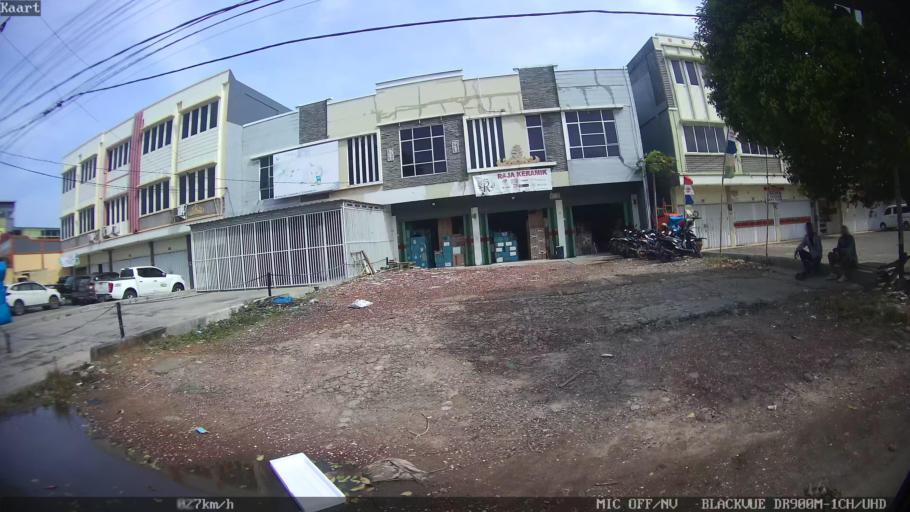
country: ID
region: Lampung
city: Kedaton
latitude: -5.3838
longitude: 105.2961
